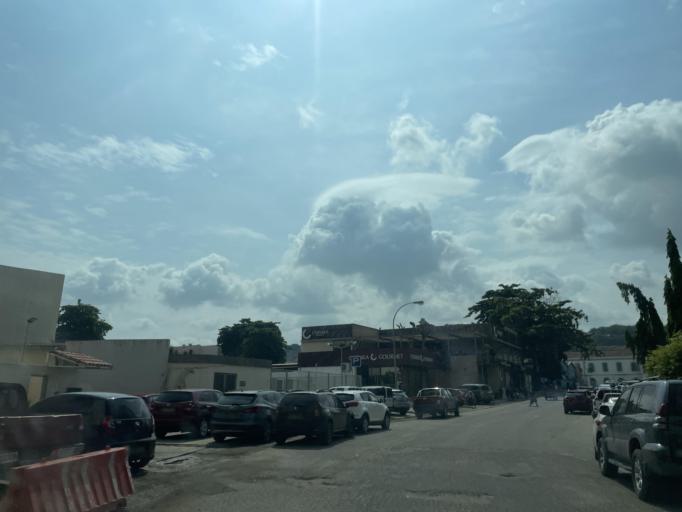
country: AO
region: Luanda
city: Luanda
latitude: -8.8039
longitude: 13.2433
